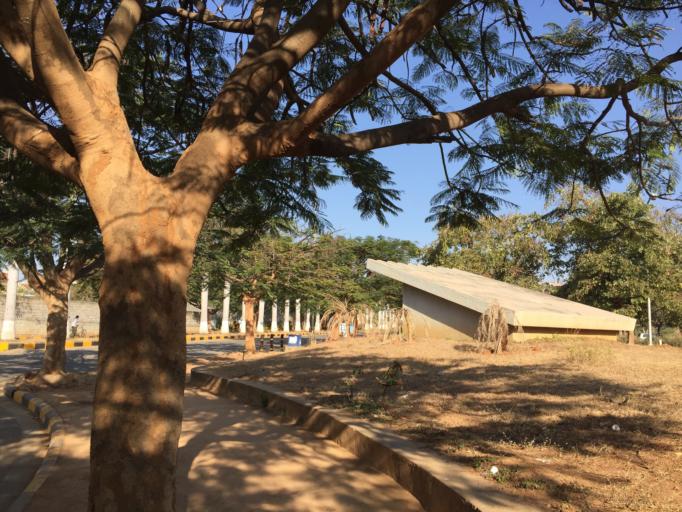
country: IN
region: Karnataka
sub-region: Bangalore Urban
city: Yelahanka
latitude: 13.0534
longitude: 77.6213
